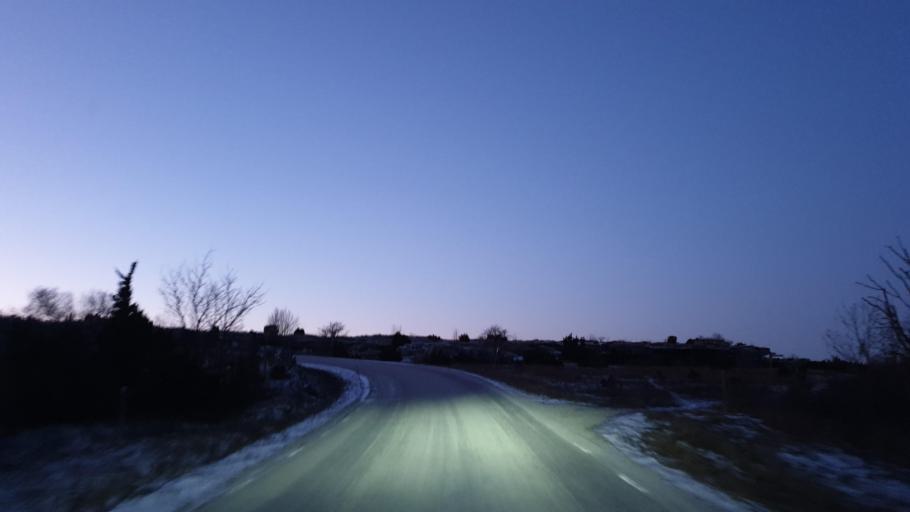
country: SE
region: Gotland
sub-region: Gotland
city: Slite
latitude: 57.4215
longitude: 18.9117
